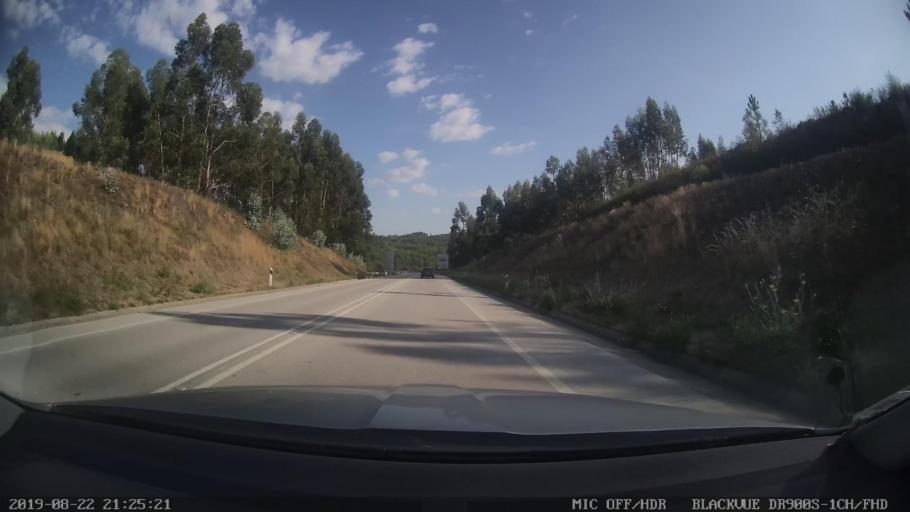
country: PT
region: Castelo Branco
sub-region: Serta
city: Serta
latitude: 39.8524
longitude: -8.1236
